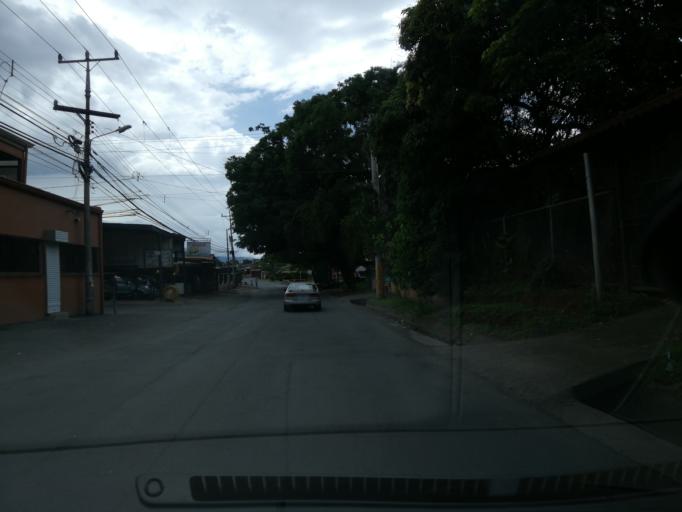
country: CR
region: Alajuela
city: Alajuela
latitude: 9.9928
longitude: -84.2336
